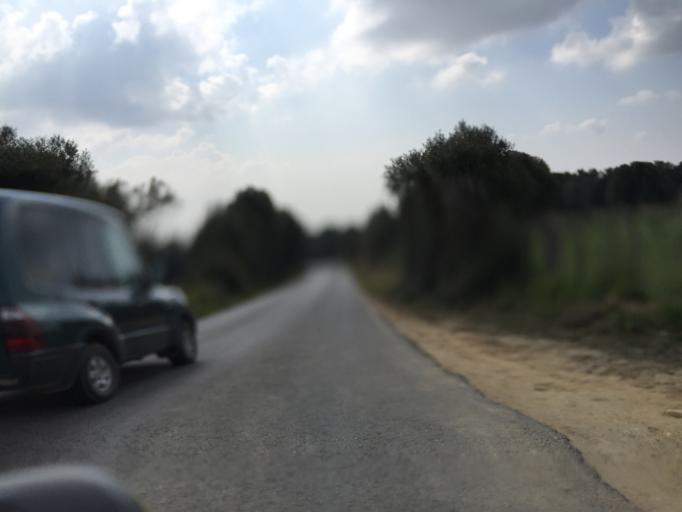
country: ES
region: Andalusia
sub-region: Provincia de Cadiz
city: Vejer de la Frontera
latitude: 36.2854
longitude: -5.9345
